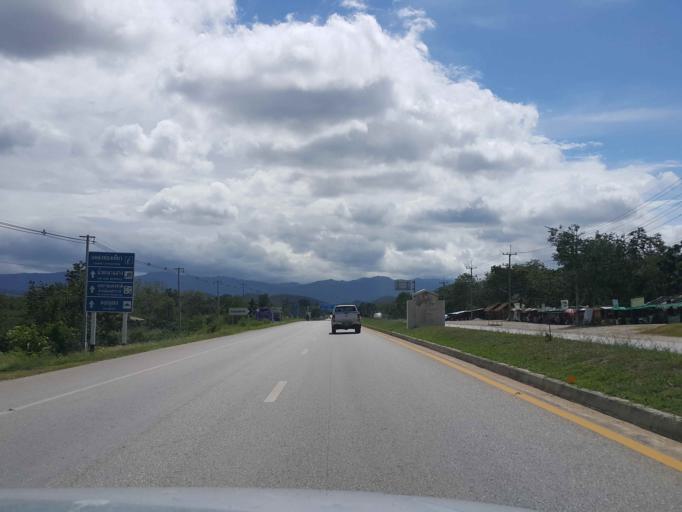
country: TH
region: Tak
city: Tak
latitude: 16.8395
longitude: 99.1102
